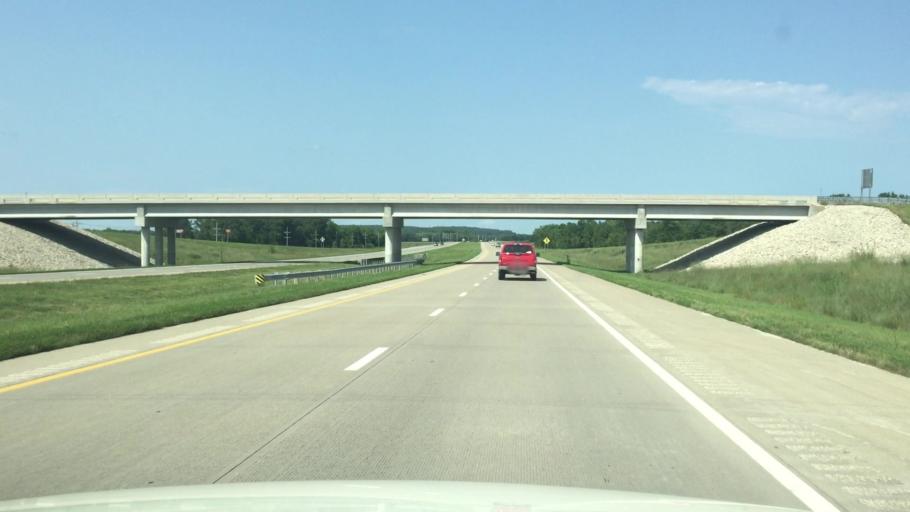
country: US
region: Kansas
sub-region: Linn County
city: Pleasanton
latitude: 38.2170
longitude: -94.7014
